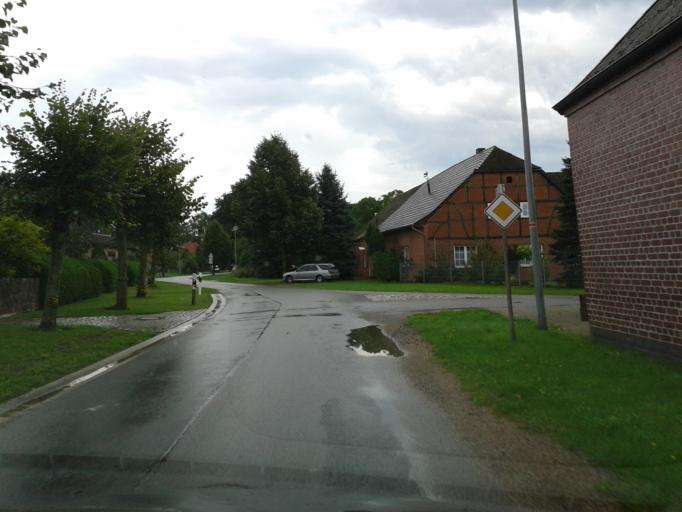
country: DE
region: Lower Saxony
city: Woltersdorf
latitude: 52.9522
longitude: 11.2088
